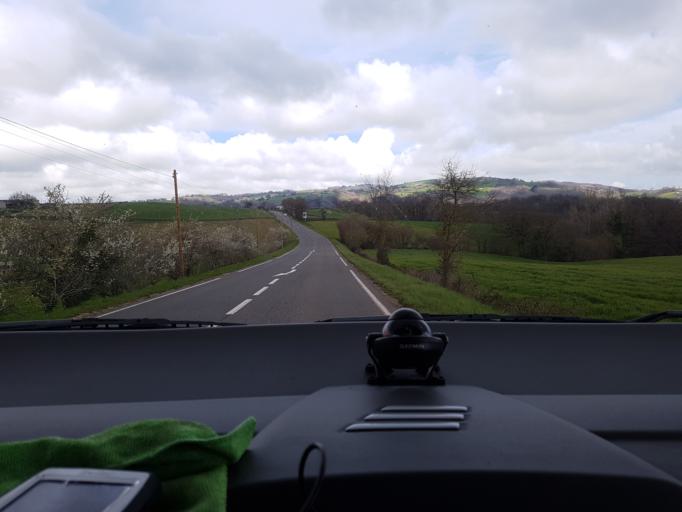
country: FR
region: Midi-Pyrenees
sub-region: Departement de l'Aveyron
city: Moyrazes
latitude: 44.3867
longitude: 2.4005
